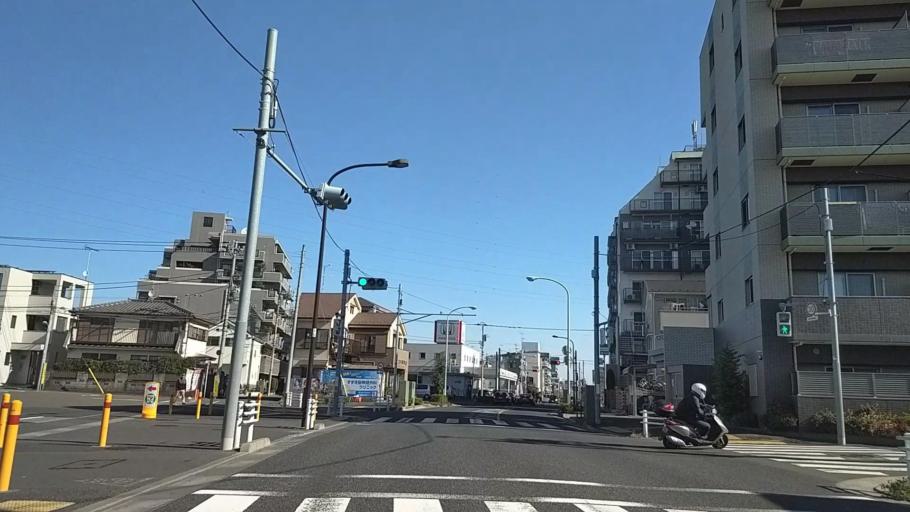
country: JP
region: Tokyo
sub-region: Machida-shi
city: Machida
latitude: 35.5515
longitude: 139.4391
